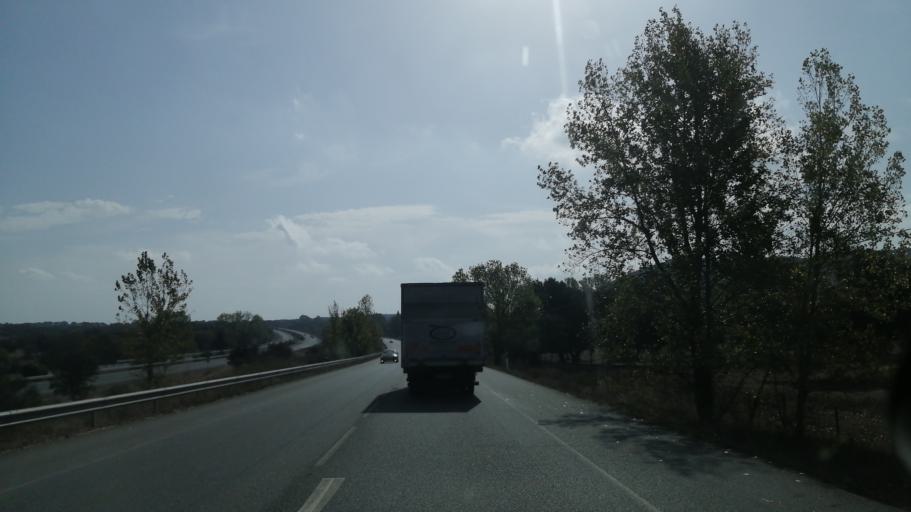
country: PT
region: Evora
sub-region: Montemor-O-Novo
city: Montemor-o-Novo
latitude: 38.6332
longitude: -8.1211
